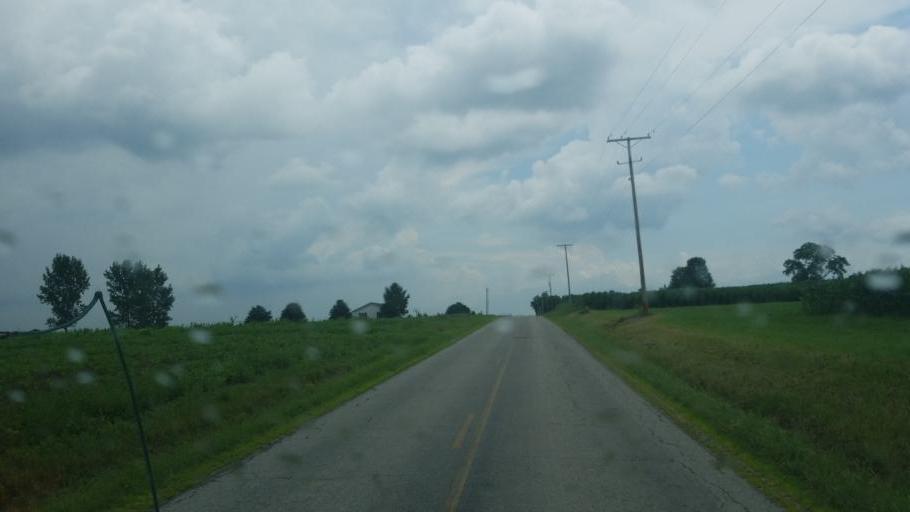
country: US
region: Ohio
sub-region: Wayne County
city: West Salem
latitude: 40.8579
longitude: -82.0927
